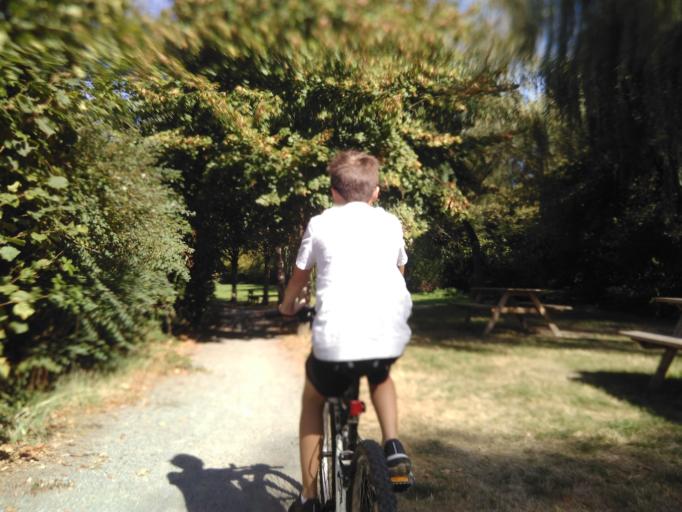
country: FR
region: Pays de la Loire
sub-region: Departement de la Vendee
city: La Chaize-le-Vicomte
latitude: 46.6713
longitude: -1.2907
